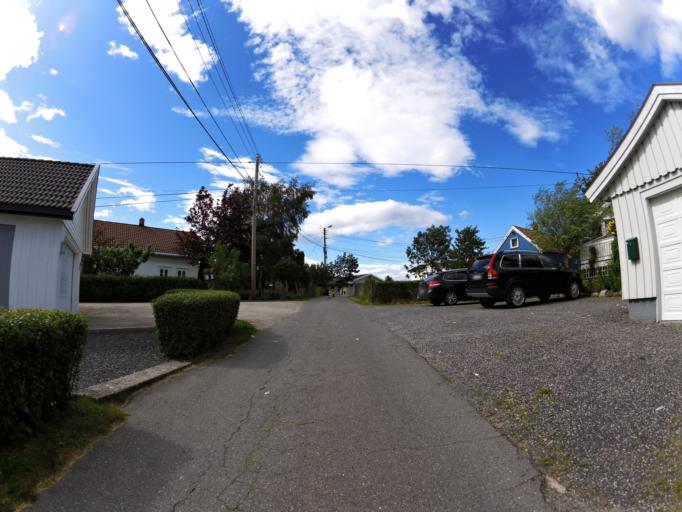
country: NO
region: Ostfold
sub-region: Fredrikstad
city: Fredrikstad
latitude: 59.2430
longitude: 11.0011
